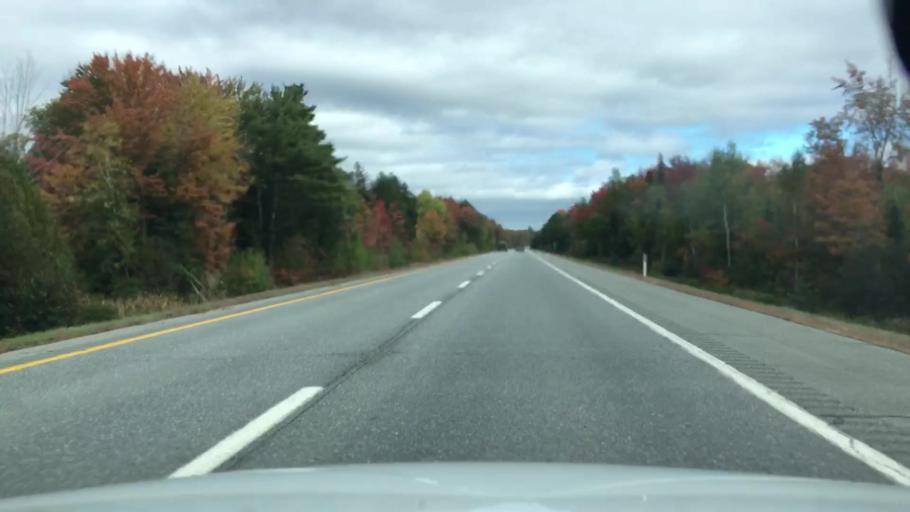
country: US
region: Maine
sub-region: Penobscot County
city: Carmel
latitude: 44.7736
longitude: -69.0273
